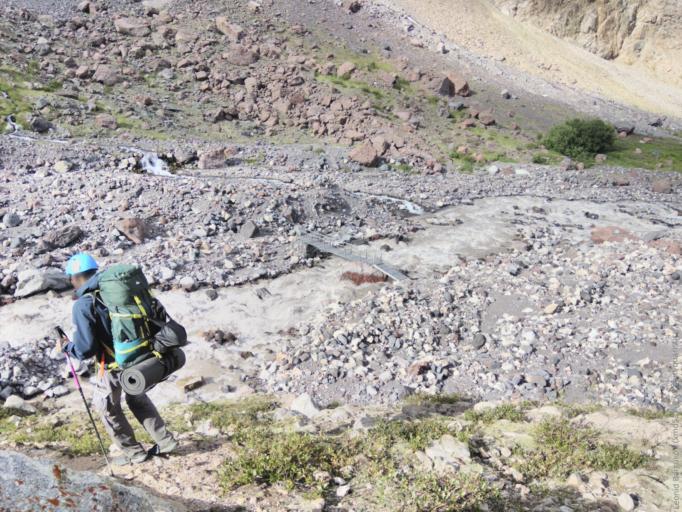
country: RU
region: Kabardino-Balkariya
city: Terskol
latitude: 43.2691
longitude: 42.4513
